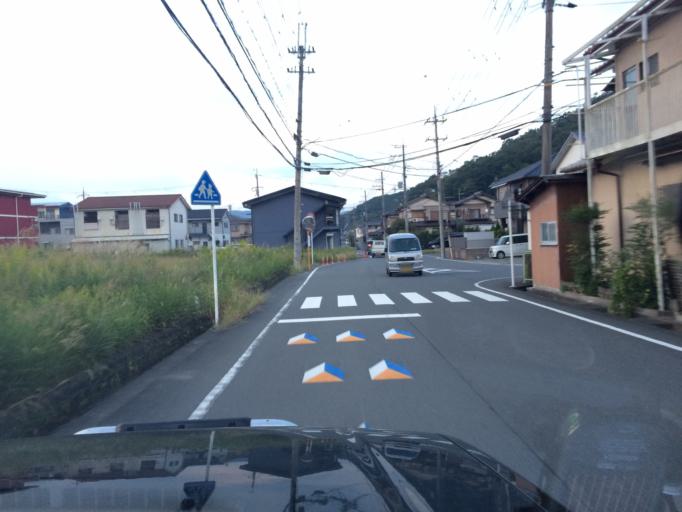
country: JP
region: Kyoto
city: Kameoka
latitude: 35.0955
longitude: 135.4748
